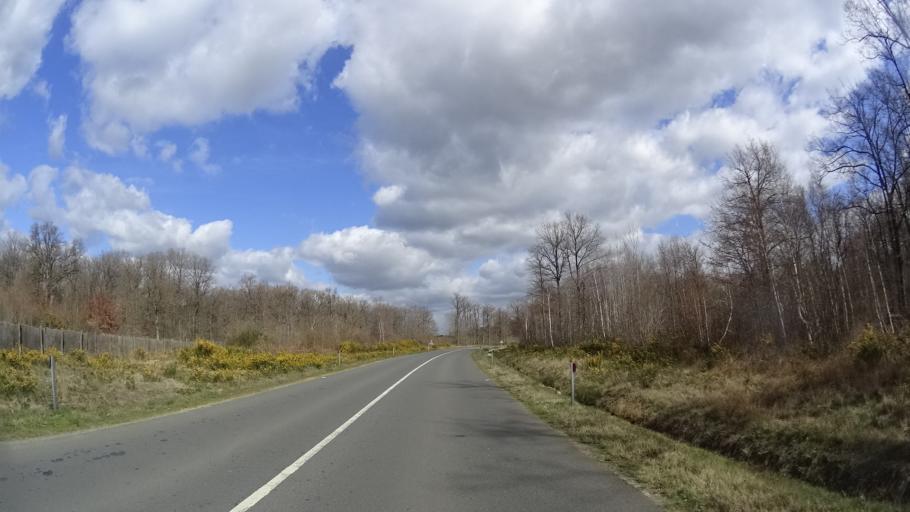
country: FR
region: Pays de la Loire
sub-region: Departement de Maine-et-Loire
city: Breze
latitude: 47.0909
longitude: -0.0028
